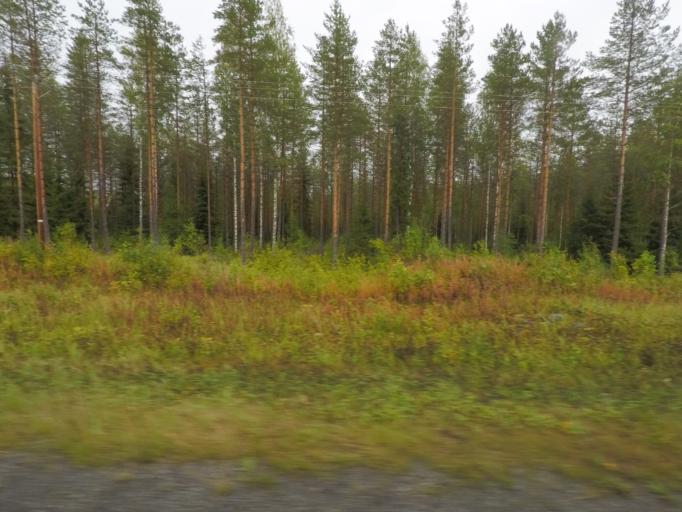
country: FI
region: Southern Savonia
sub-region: Pieksaemaeki
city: Juva
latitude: 61.9704
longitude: 27.8042
